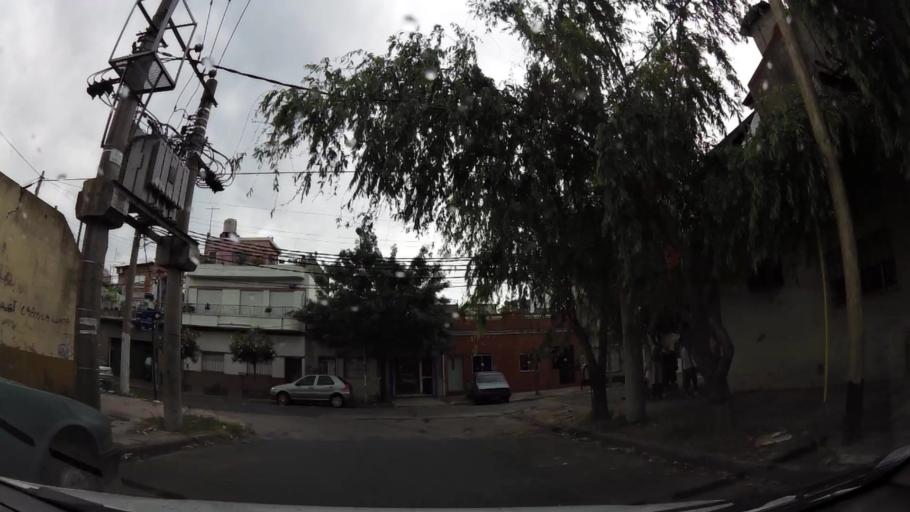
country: AR
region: Buenos Aires
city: San Justo
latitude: -34.6603
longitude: -58.5221
